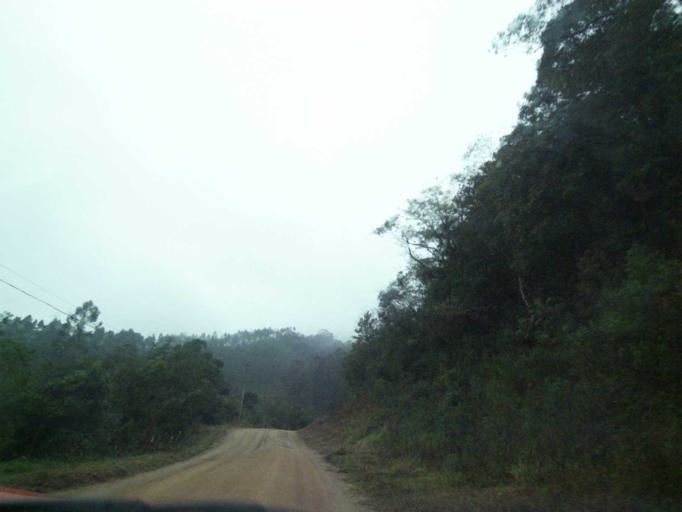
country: BR
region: Santa Catarina
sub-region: Anitapolis
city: Anitapolis
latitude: -27.9164
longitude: -49.1329
